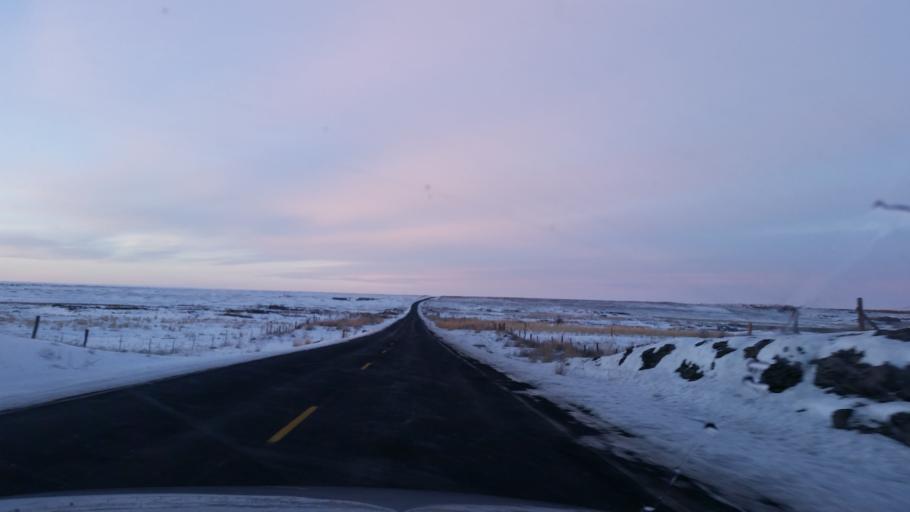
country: US
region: Washington
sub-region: Spokane County
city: Medical Lake
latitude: 47.2256
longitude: -117.9063
